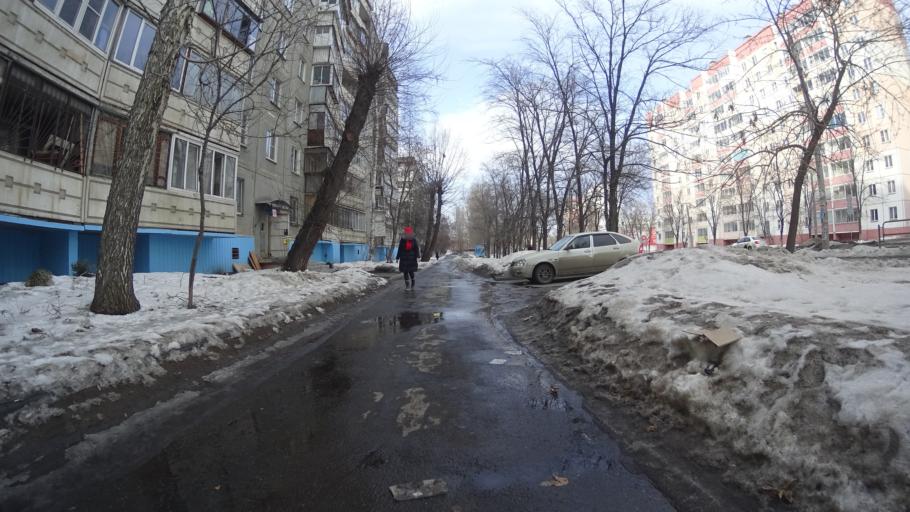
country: RU
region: Chelyabinsk
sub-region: Gorod Chelyabinsk
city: Chelyabinsk
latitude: 55.1961
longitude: 61.3176
